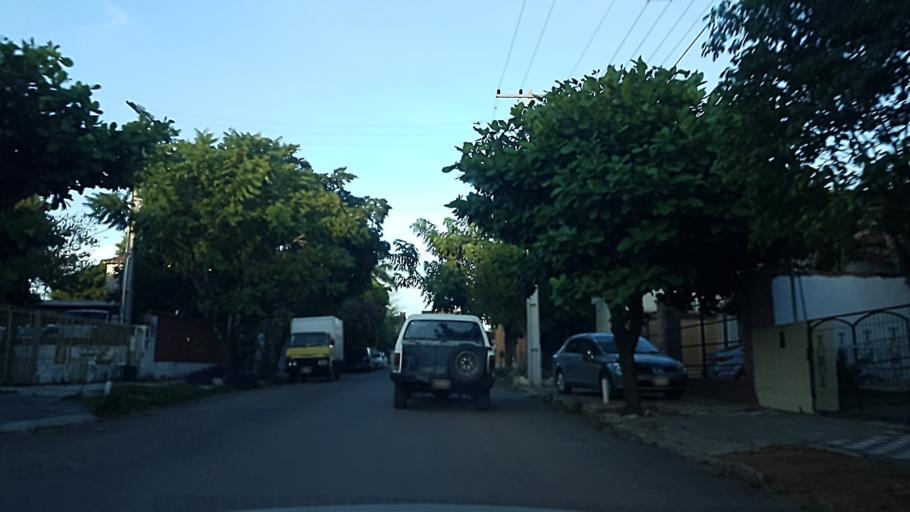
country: PY
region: Asuncion
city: Asuncion
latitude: -25.2678
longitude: -57.5872
